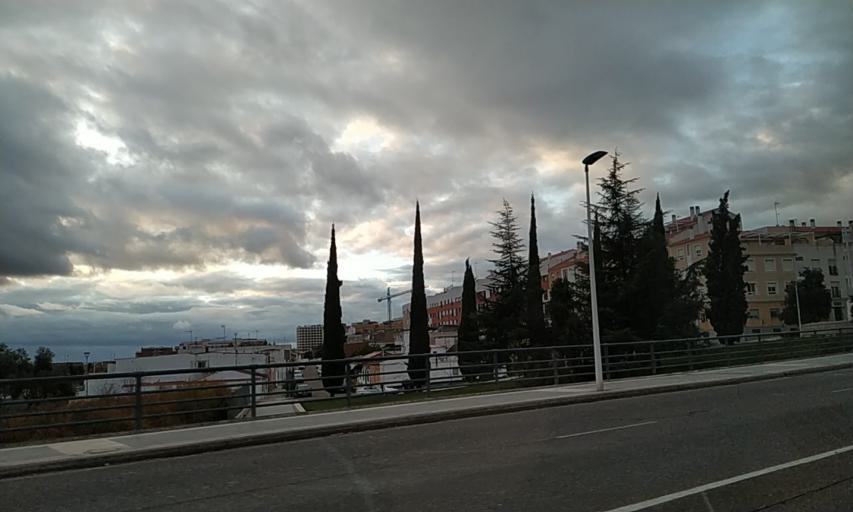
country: ES
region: Extremadura
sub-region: Provincia de Badajoz
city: Badajoz
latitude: 38.8854
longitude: -6.9747
